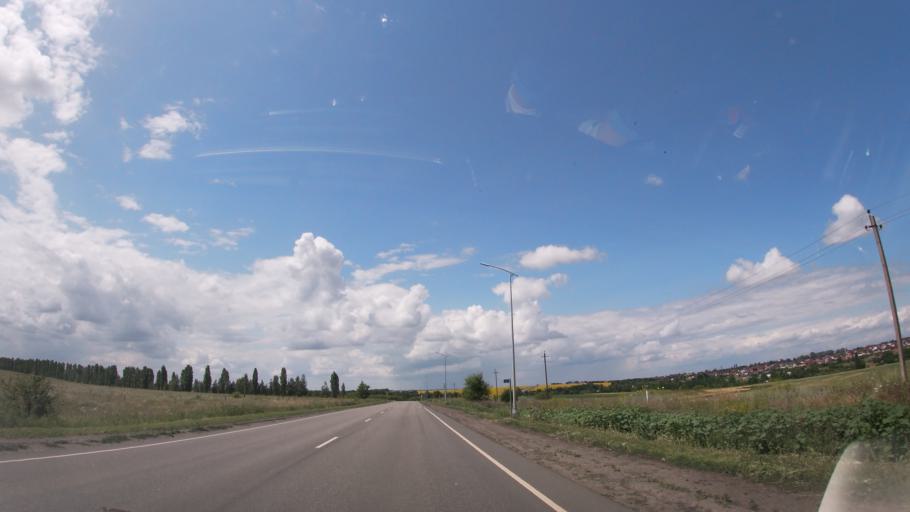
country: RU
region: Belgorod
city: Severnyy
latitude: 50.6655
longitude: 36.5334
